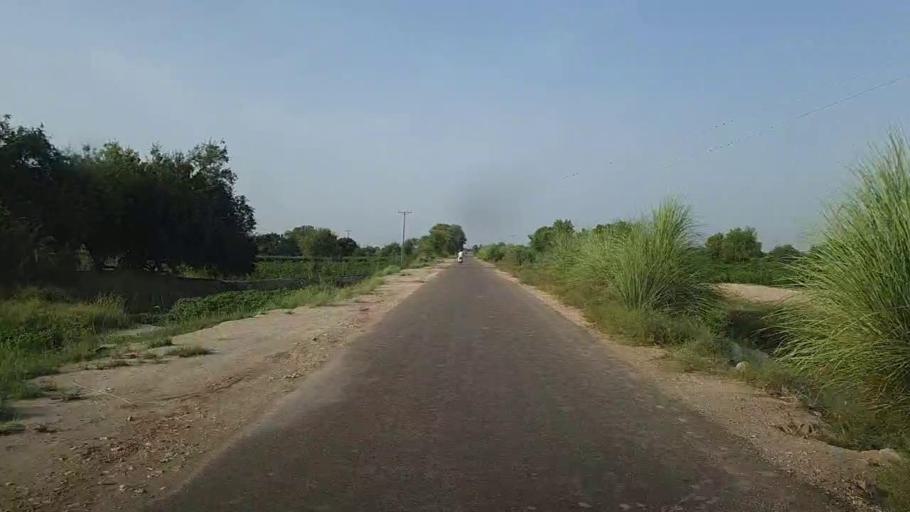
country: PK
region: Sindh
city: Khairpur
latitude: 28.0841
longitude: 69.8160
